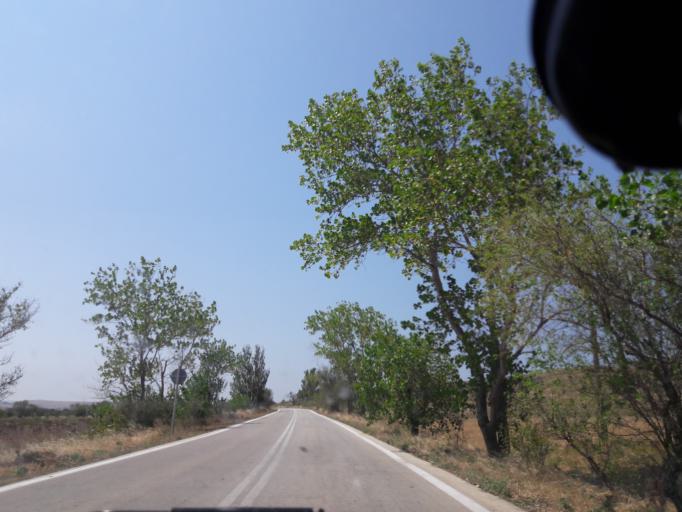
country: GR
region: North Aegean
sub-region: Nomos Lesvou
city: Myrina
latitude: 39.9238
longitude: 25.3292
